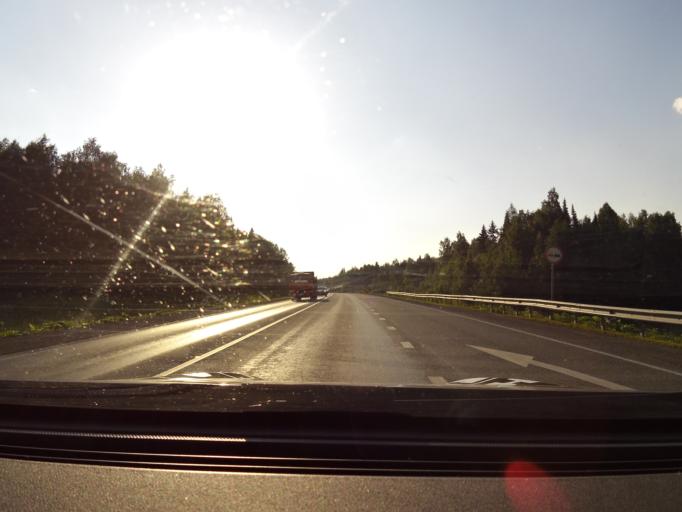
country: RU
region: Sverdlovsk
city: Bilimbay
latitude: 56.8498
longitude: 59.8094
